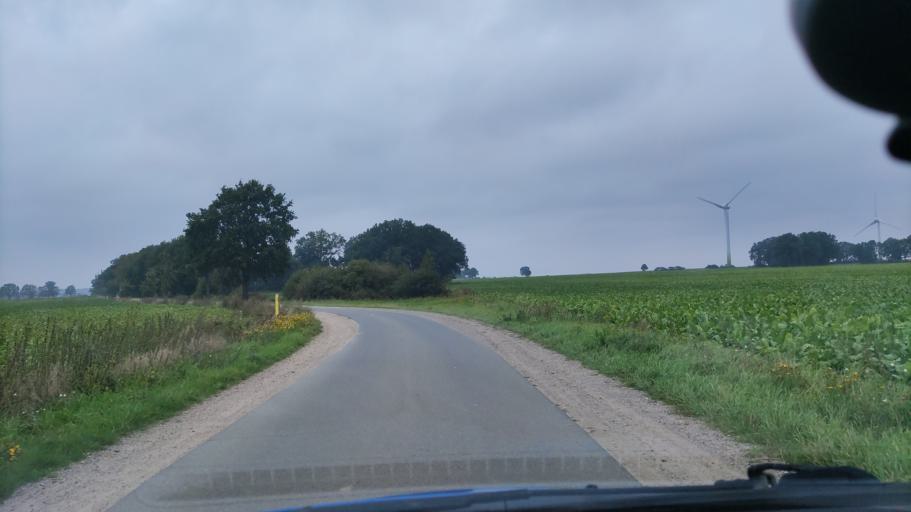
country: DE
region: Lower Saxony
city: Altenmedingen
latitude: 53.1209
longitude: 10.6278
